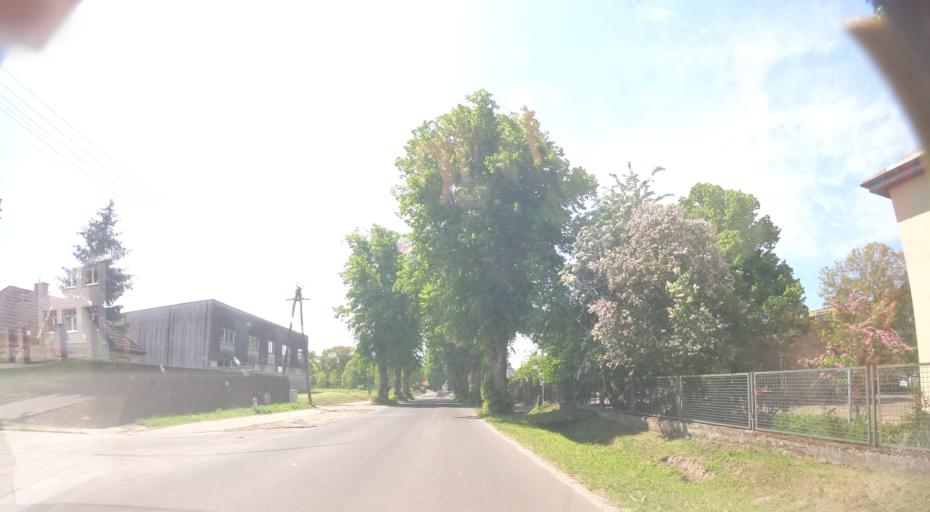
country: PL
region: West Pomeranian Voivodeship
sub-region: Powiat kolobrzeski
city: Dygowo
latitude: 54.1348
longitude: 15.7266
